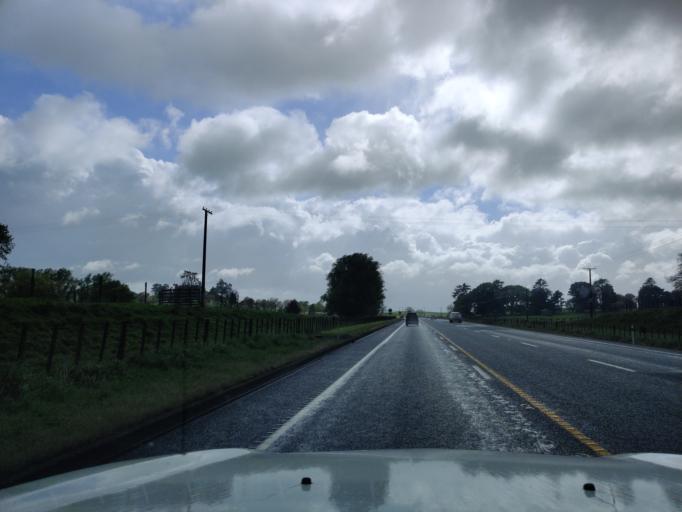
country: NZ
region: Waikato
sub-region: Matamata-Piako District
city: Matamata
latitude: -37.9847
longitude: 175.7311
